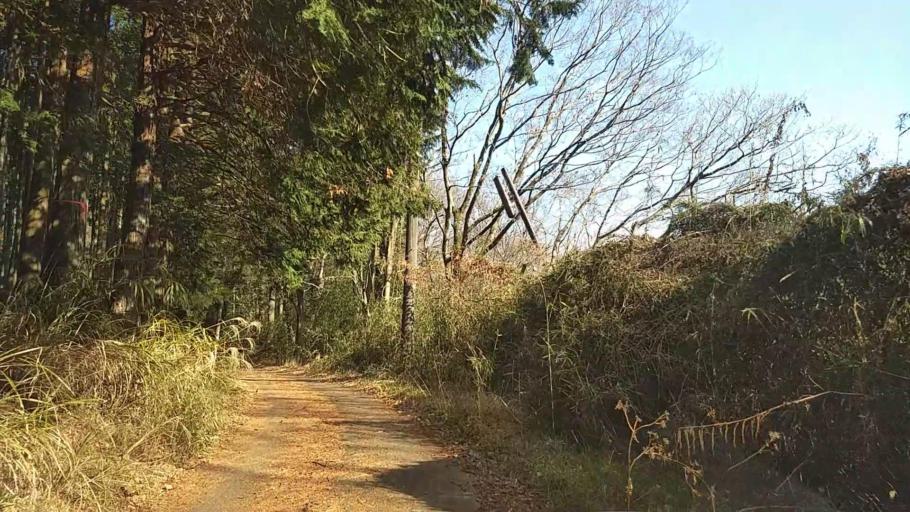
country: JP
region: Kanagawa
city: Isehara
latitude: 35.4428
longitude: 139.2901
